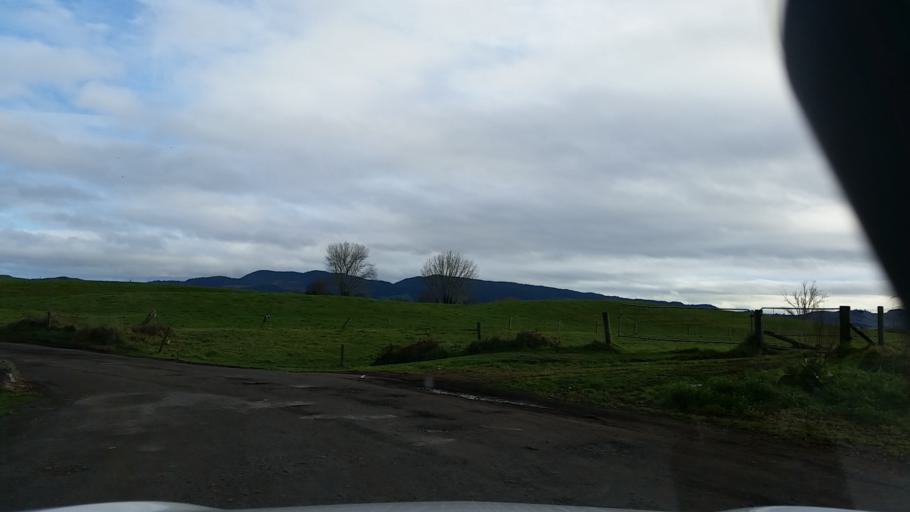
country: NZ
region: Bay of Plenty
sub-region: Rotorua District
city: Rotorua
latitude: -38.4530
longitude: 176.3429
